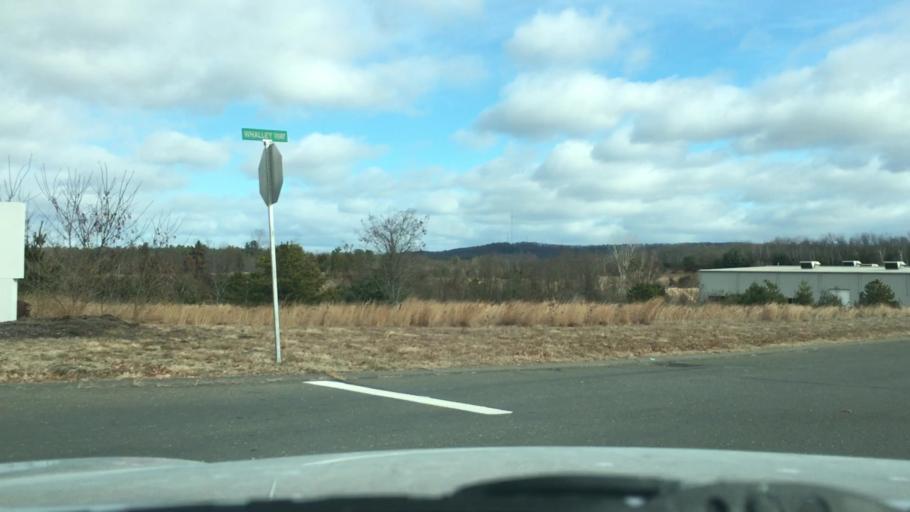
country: US
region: Massachusetts
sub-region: Hampden County
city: Southwick
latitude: 42.0702
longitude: -72.7449
